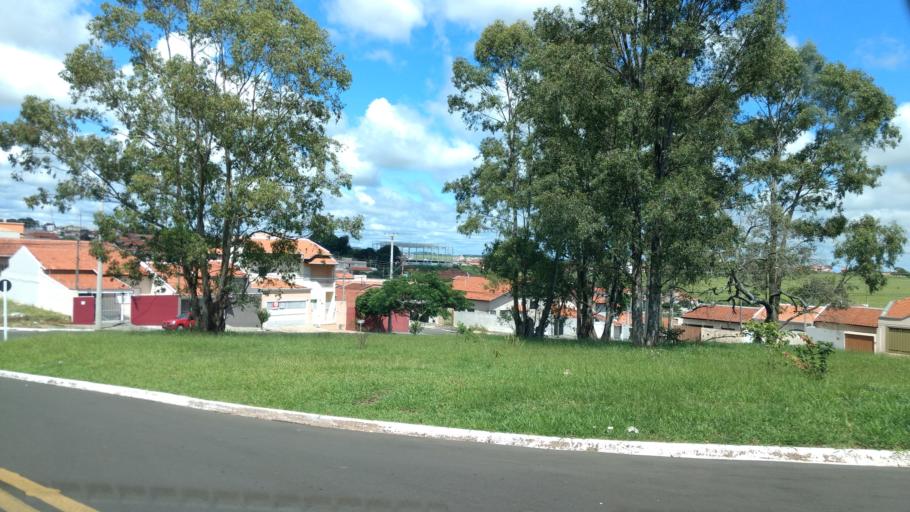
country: BR
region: Sao Paulo
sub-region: Botucatu
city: Botucatu
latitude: -22.8545
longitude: -48.4434
